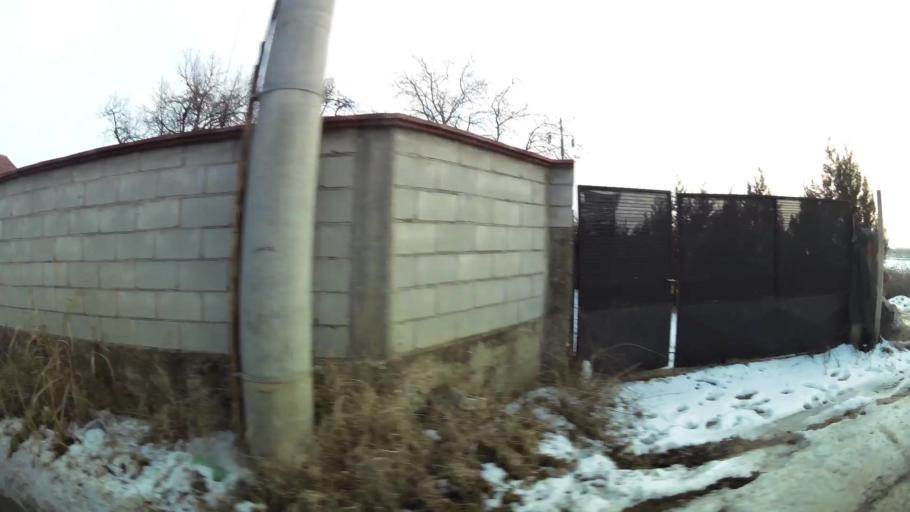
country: MK
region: Aracinovo
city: Arachinovo
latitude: 42.0191
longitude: 21.5613
